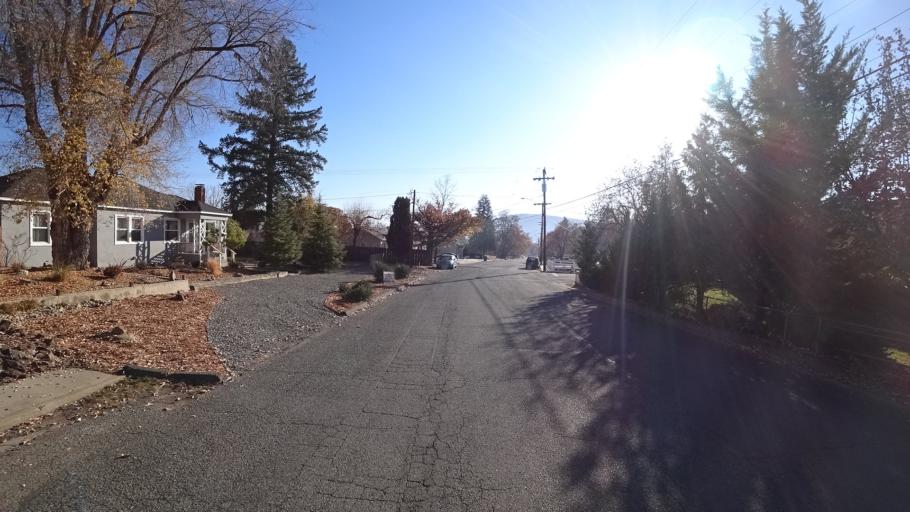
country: US
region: California
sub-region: Siskiyou County
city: Yreka
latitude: 41.7391
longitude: -122.6444
